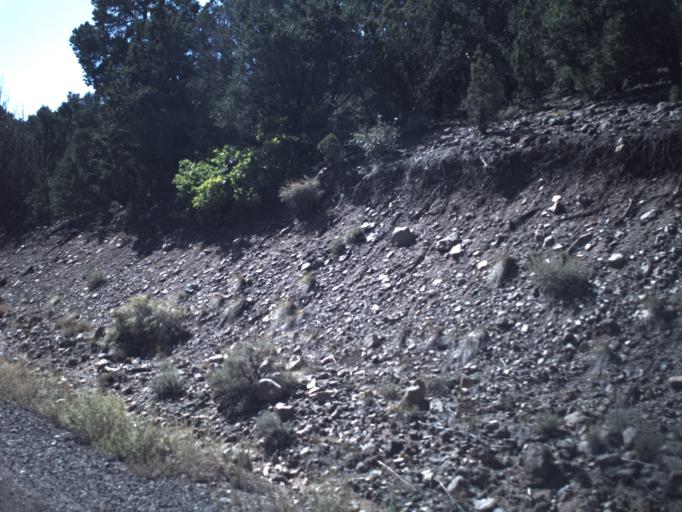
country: US
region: Utah
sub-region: Piute County
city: Junction
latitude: 38.2598
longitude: -112.3062
